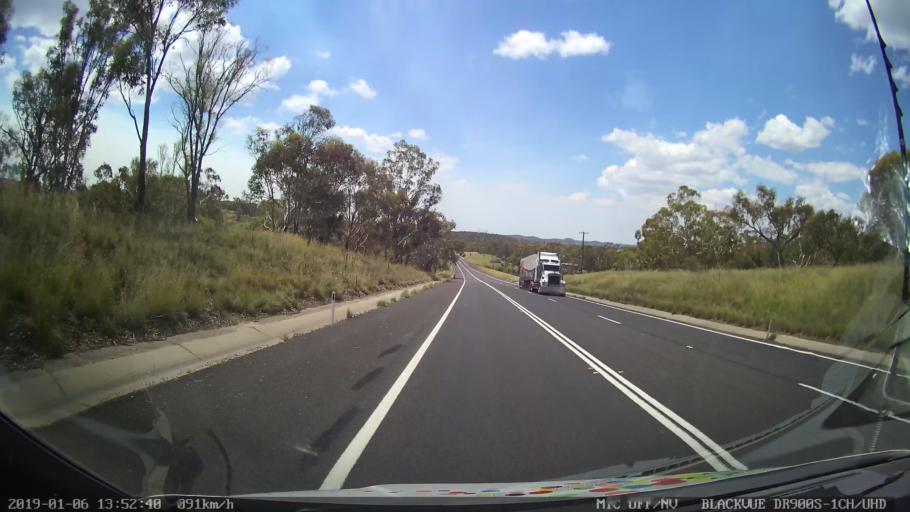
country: AU
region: New South Wales
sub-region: Tamworth Municipality
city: Kootingal
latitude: -30.9176
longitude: 151.1337
